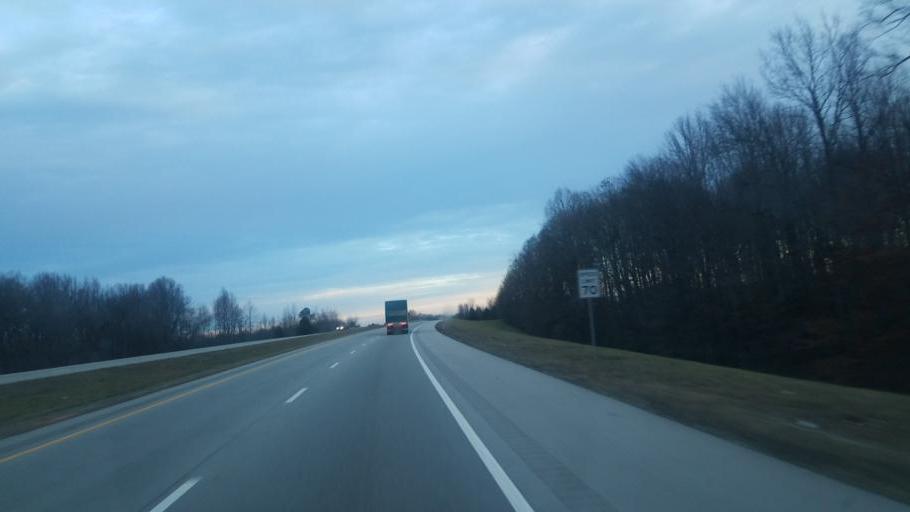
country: US
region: Tennessee
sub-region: White County
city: Sparta
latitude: 36.0286
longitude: -85.5086
